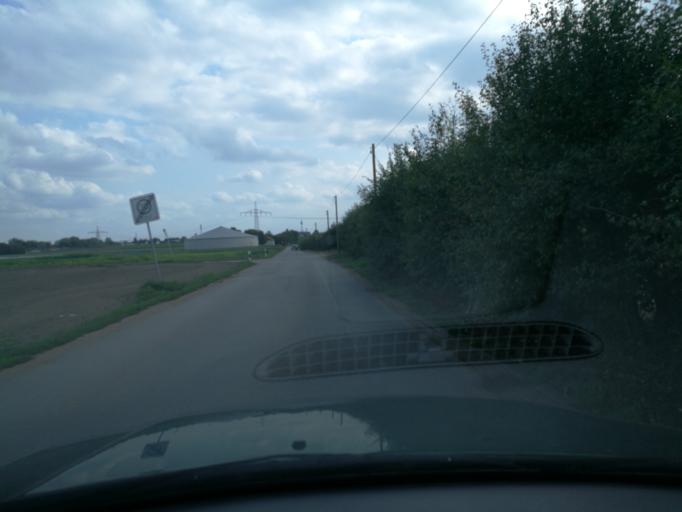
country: DE
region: Bavaria
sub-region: Regierungsbezirk Mittelfranken
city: Wetzendorf
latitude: 49.4881
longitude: 11.0281
